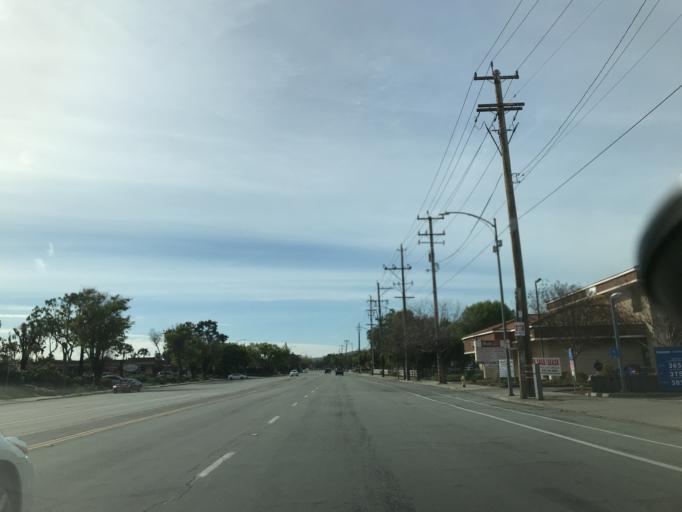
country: US
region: California
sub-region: Santa Clara County
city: Alum Rock
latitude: 37.3247
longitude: -121.7970
